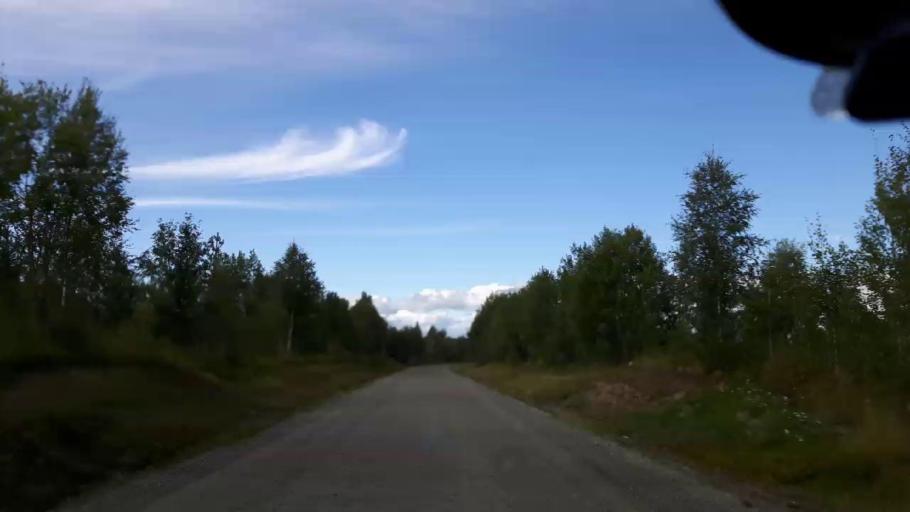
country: SE
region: Jaemtland
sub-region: Ragunda Kommun
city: Hammarstrand
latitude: 63.1314
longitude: 15.9549
